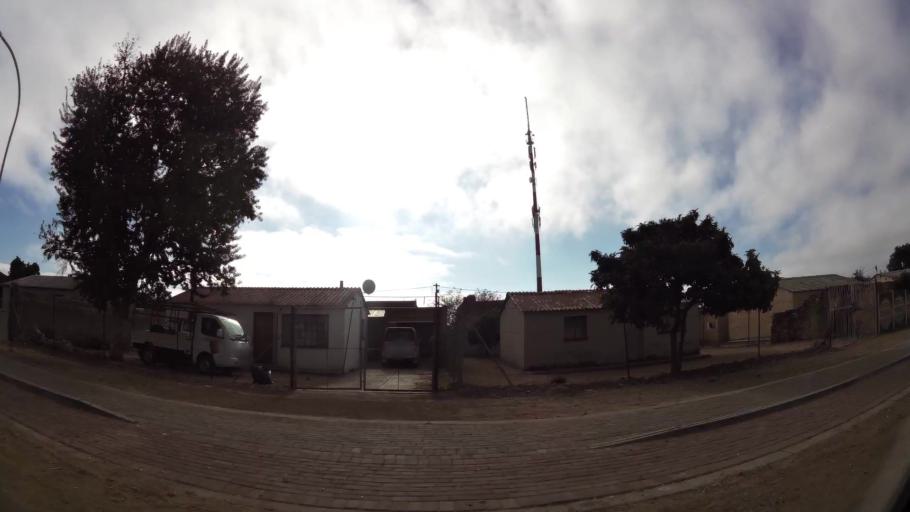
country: ZA
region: Limpopo
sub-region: Capricorn District Municipality
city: Polokwane
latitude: -23.8464
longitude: 29.3890
